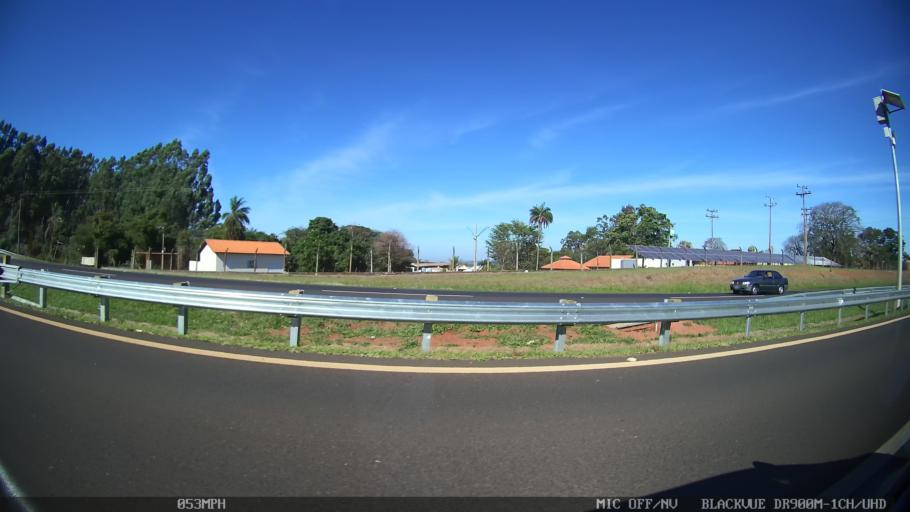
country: BR
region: Sao Paulo
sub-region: Franca
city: Franca
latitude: -20.5760
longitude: -47.3565
